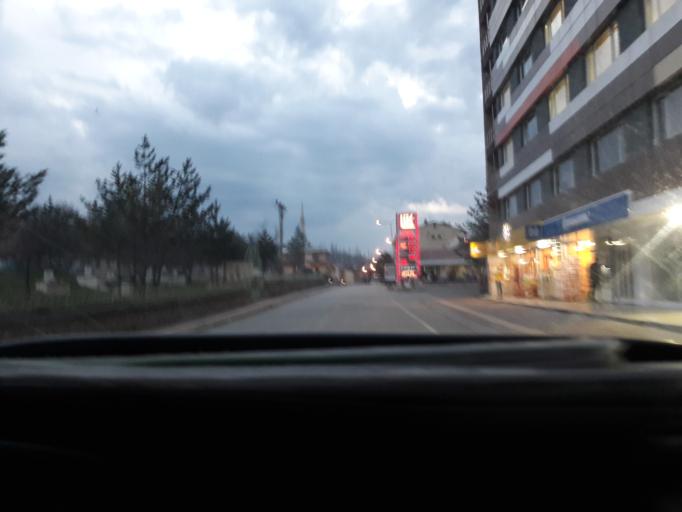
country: TR
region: Giresun
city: Alucra
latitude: 40.3225
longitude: 38.7617
